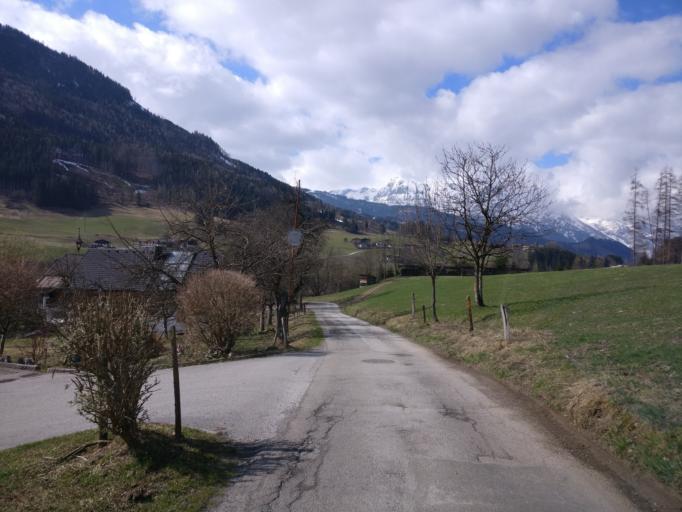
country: AT
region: Salzburg
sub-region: Politischer Bezirk Sankt Johann im Pongau
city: Pfarrwerfen
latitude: 47.4406
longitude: 13.2162
